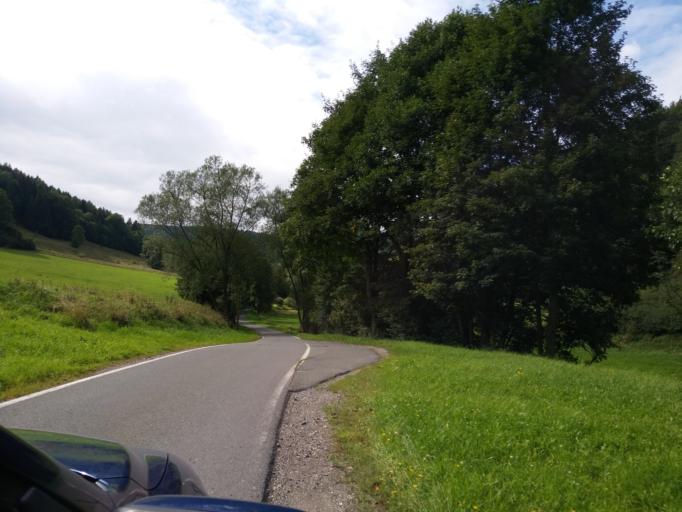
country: DE
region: Thuringia
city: Grafenthal
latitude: 50.5437
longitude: 11.3307
